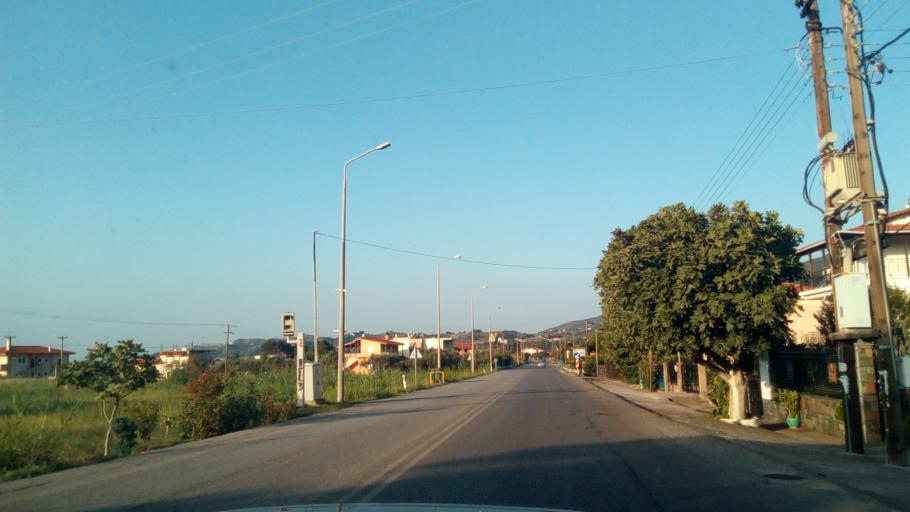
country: GR
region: West Greece
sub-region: Nomos Aitolias kai Akarnanias
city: Nafpaktos
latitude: 38.3787
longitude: 21.7950
